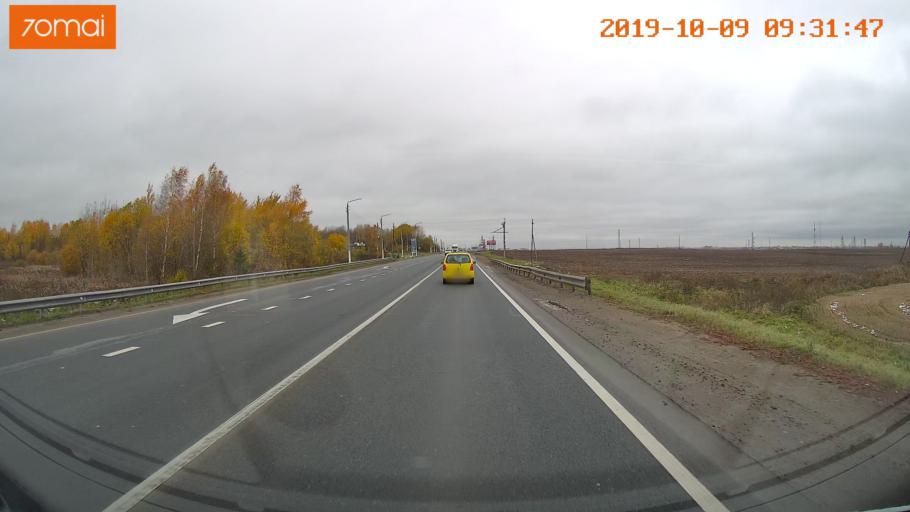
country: RU
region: Vologda
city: Vologda
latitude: 59.1526
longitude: 39.9353
